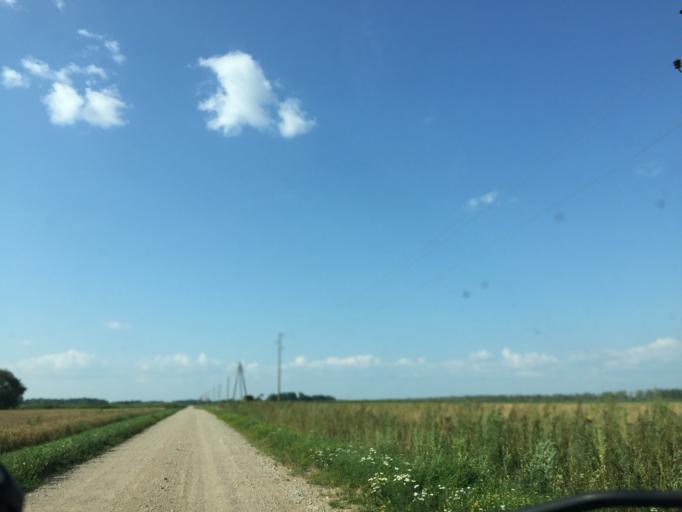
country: LV
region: Jelgava
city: Jelgava
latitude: 56.4643
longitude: 23.6803
